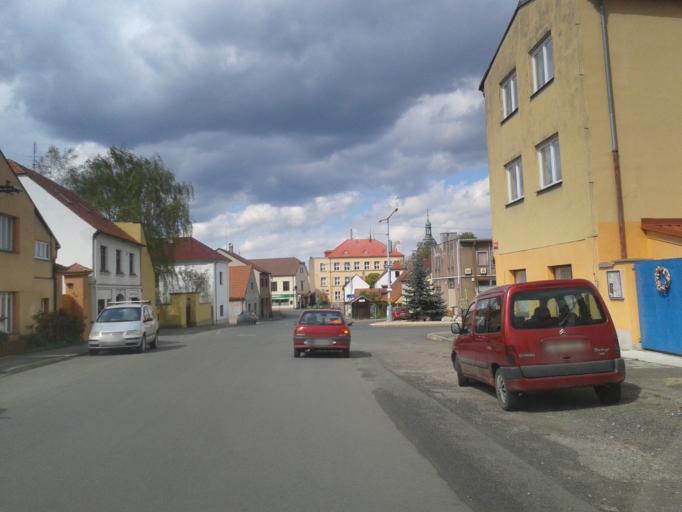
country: CZ
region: Central Bohemia
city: Revnice
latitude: 49.9034
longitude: 14.1467
